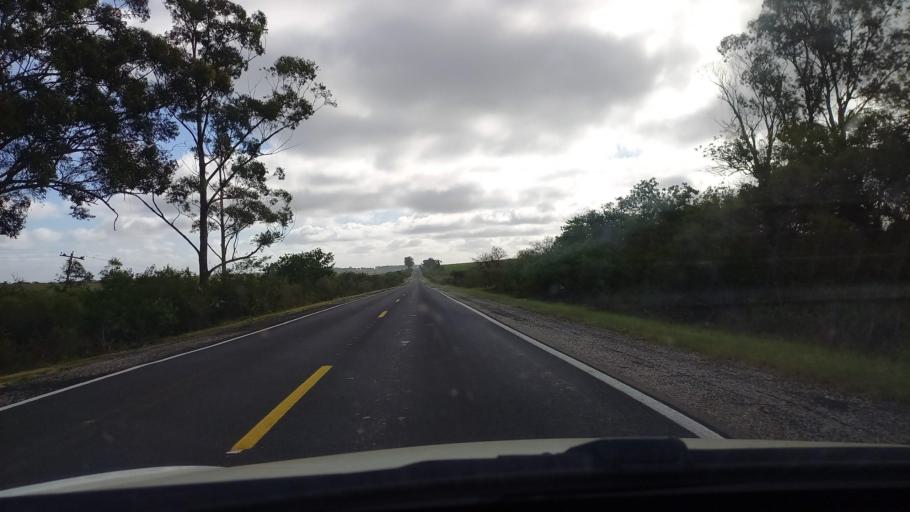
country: BR
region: Rio Grande do Sul
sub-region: Dom Pedrito
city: Dom Pedrito
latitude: -30.8977
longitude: -54.8427
